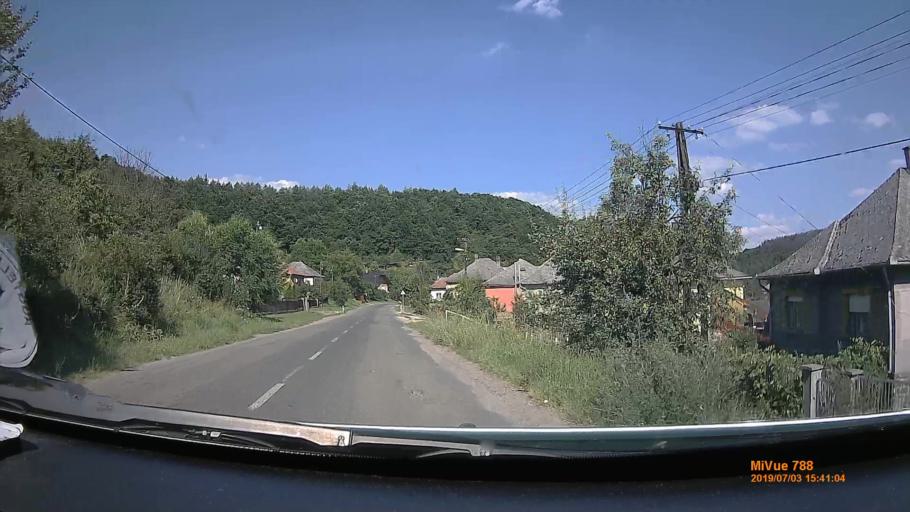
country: HU
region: Heves
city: Szilvasvarad
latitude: 48.1676
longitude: 20.4184
